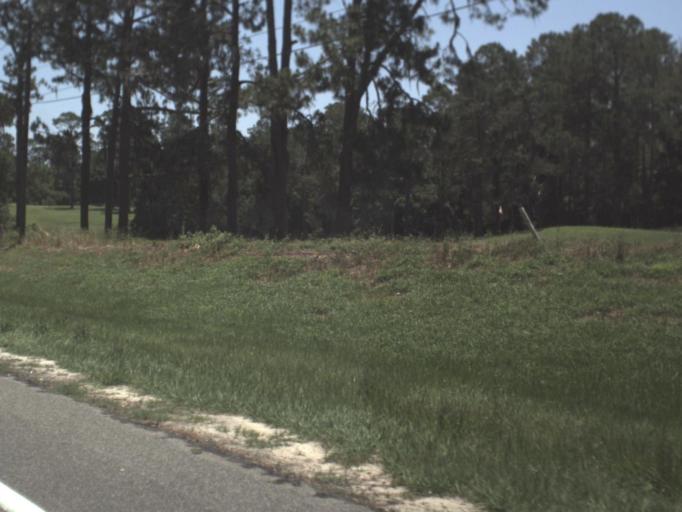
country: US
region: Florida
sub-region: Suwannee County
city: Live Oak
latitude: 30.2617
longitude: -82.9114
